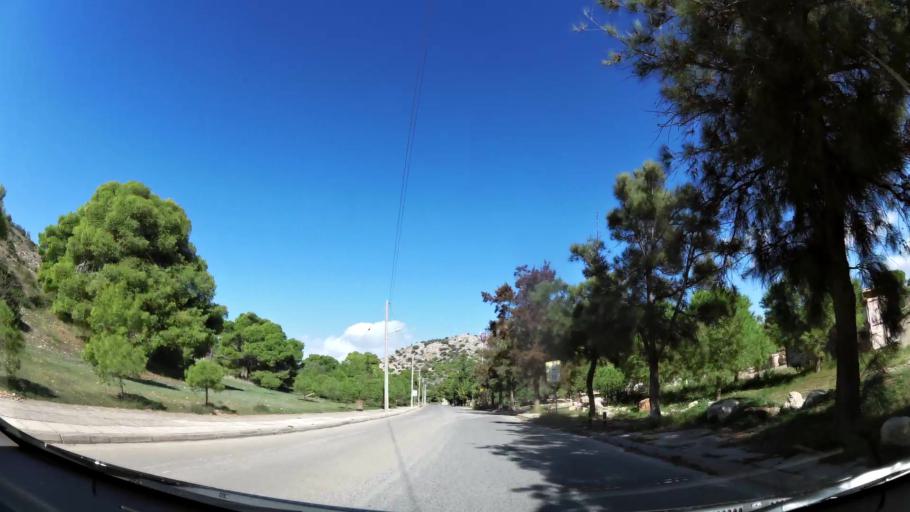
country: GR
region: Attica
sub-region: Nomarchia Anatolikis Attikis
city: Vouliagmeni
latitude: 37.8132
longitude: 23.7903
